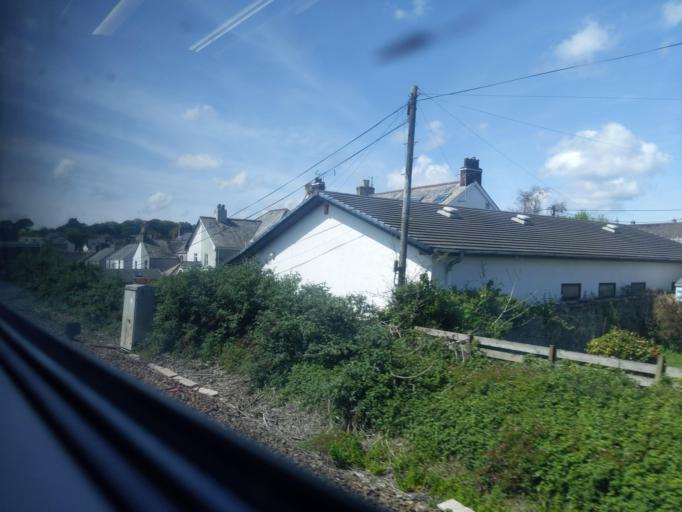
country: GB
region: England
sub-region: Cornwall
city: St Austell
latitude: 50.3391
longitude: -4.7749
